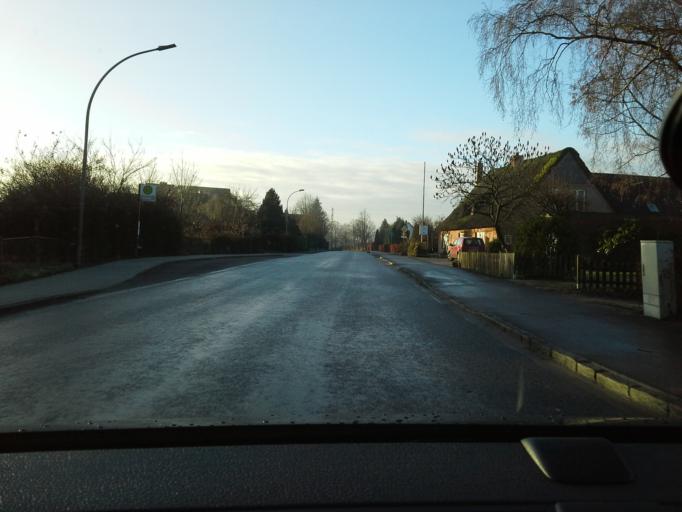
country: DE
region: Schleswig-Holstein
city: Borstel-Hohenraden
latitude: 53.6849
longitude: 9.8070
